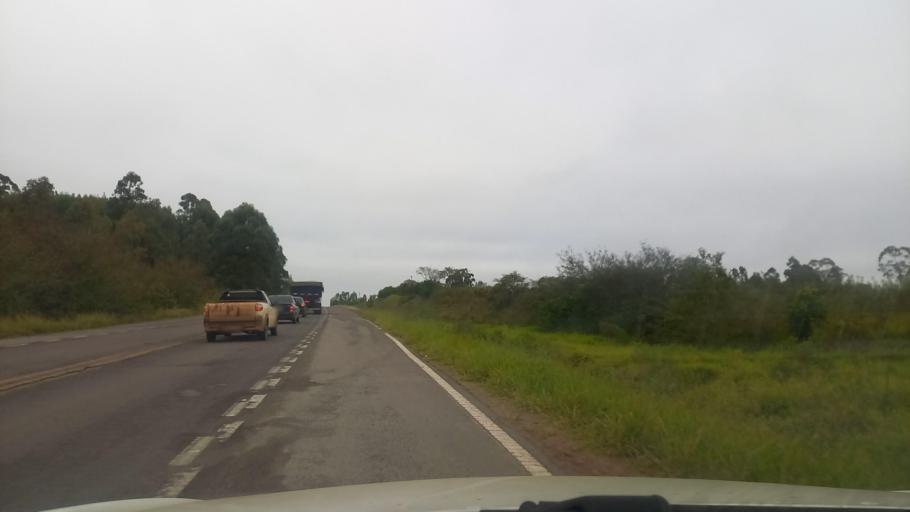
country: BR
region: Rio Grande do Sul
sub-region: Sao Pedro Do Sul
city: Sao Pedro do Sul
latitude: -29.7720
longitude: -54.0954
